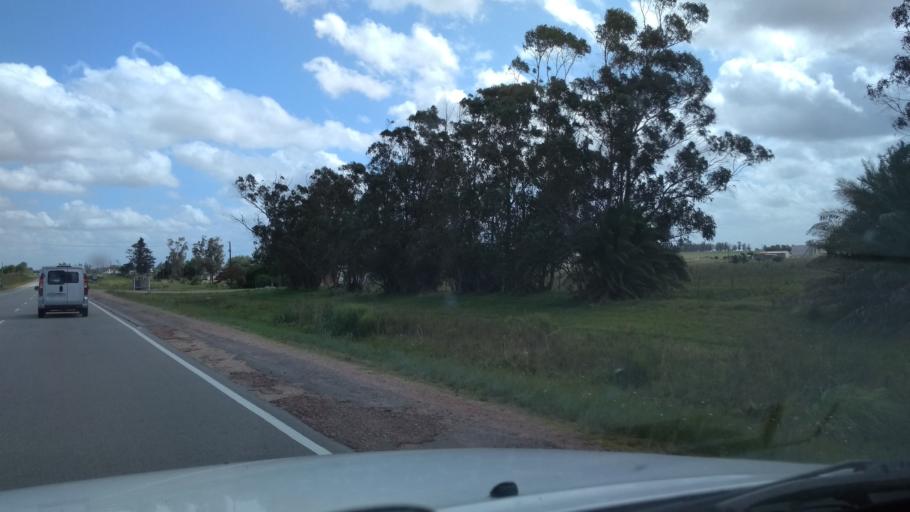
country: UY
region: Canelones
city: Santa Rosa
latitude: -34.5367
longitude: -56.0568
